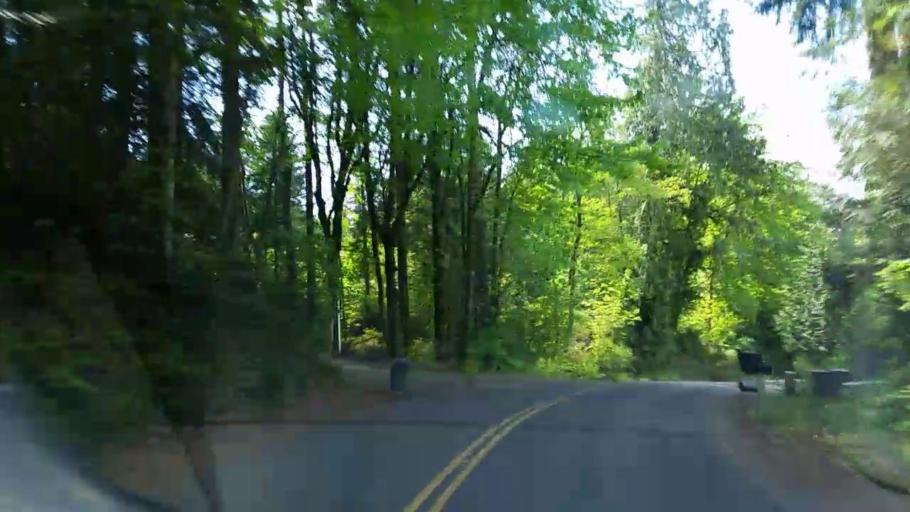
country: US
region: Washington
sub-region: Pierce County
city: Key Center
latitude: 47.3371
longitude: -122.7663
